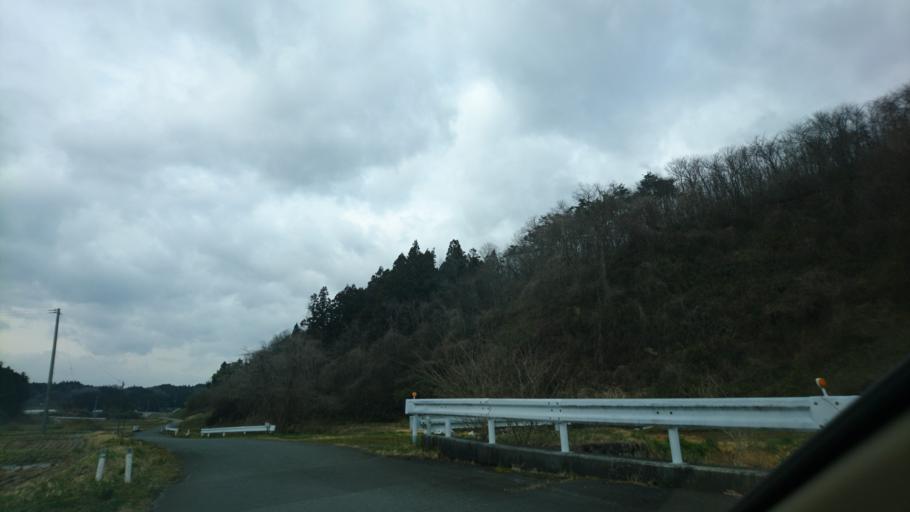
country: JP
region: Iwate
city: Ichinoseki
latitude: 38.8959
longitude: 141.1834
